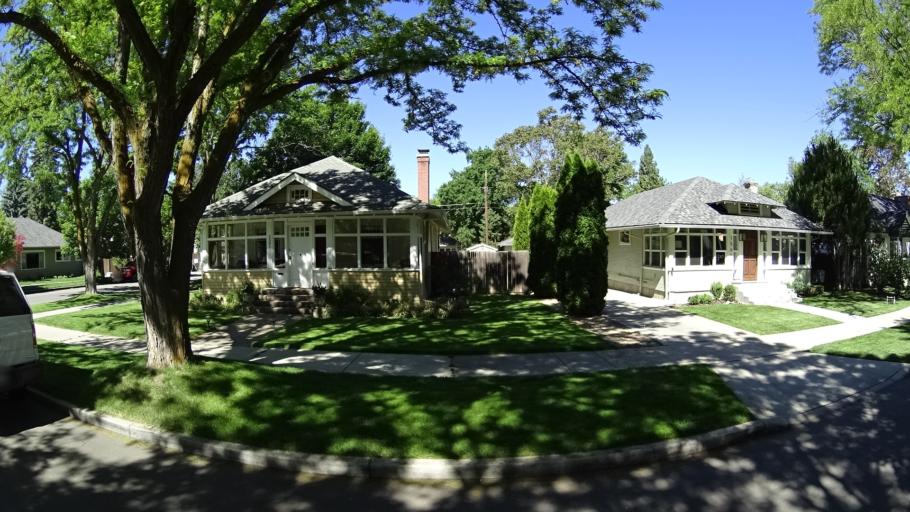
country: US
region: Idaho
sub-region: Ada County
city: Boise
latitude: 43.6340
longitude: -116.2133
